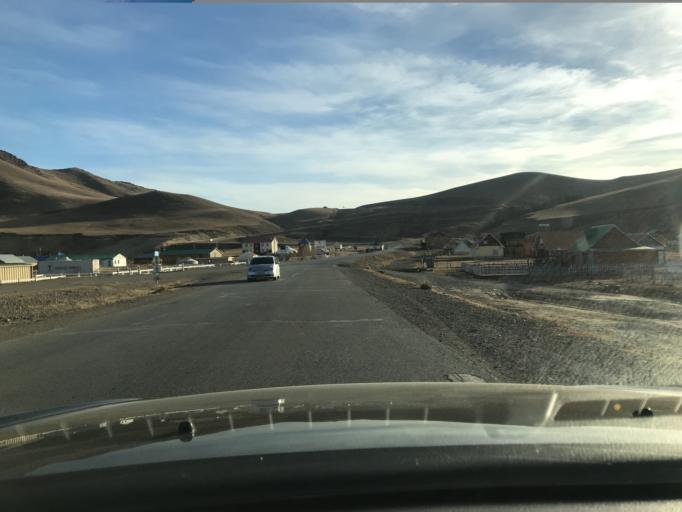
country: MN
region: Central Aimak
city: Dzuunmod
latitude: 47.8193
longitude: 107.3306
